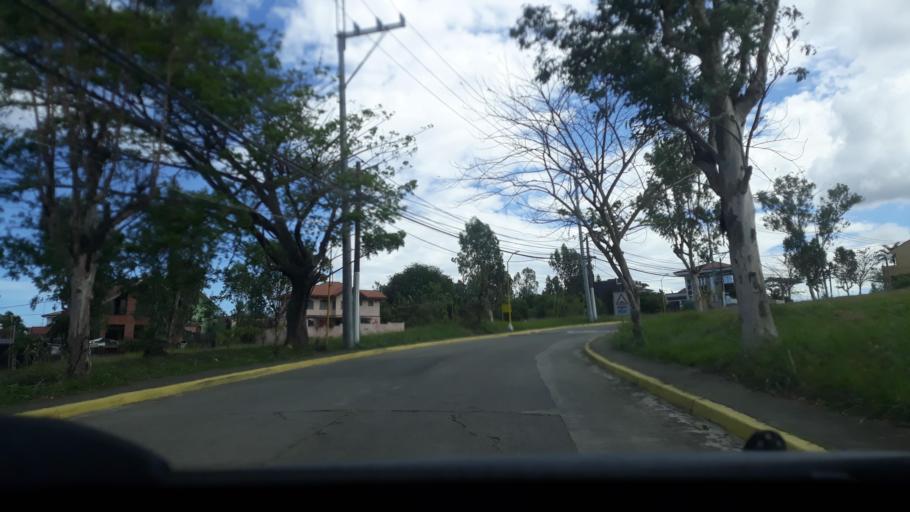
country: PH
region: Calabarzon
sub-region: Province of Cavite
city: Bulihan
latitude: 14.3038
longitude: 120.9673
